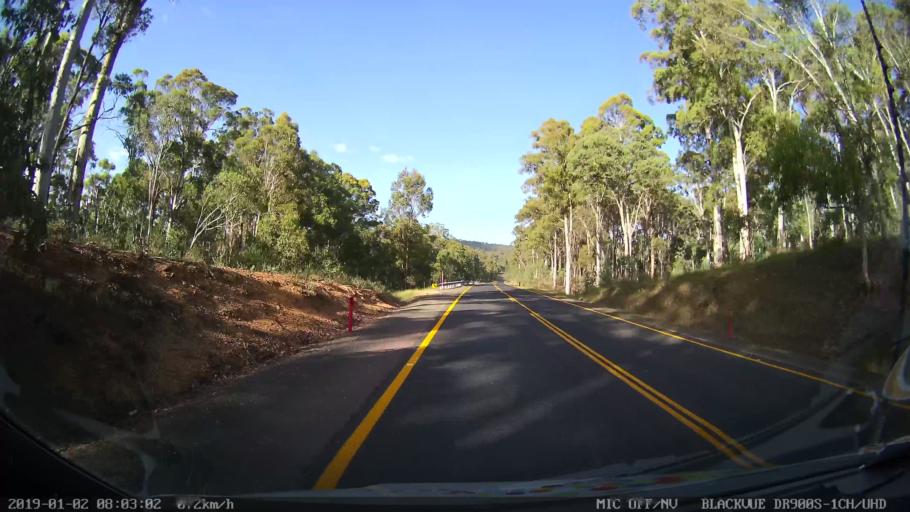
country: AU
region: New South Wales
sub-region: Tumut Shire
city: Tumut
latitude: -35.6608
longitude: 148.4140
